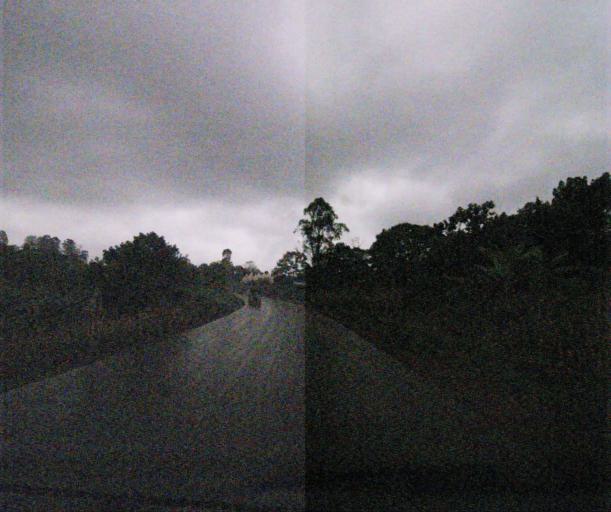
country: CM
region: West
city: Bansoa
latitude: 5.4737
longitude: 10.2876
